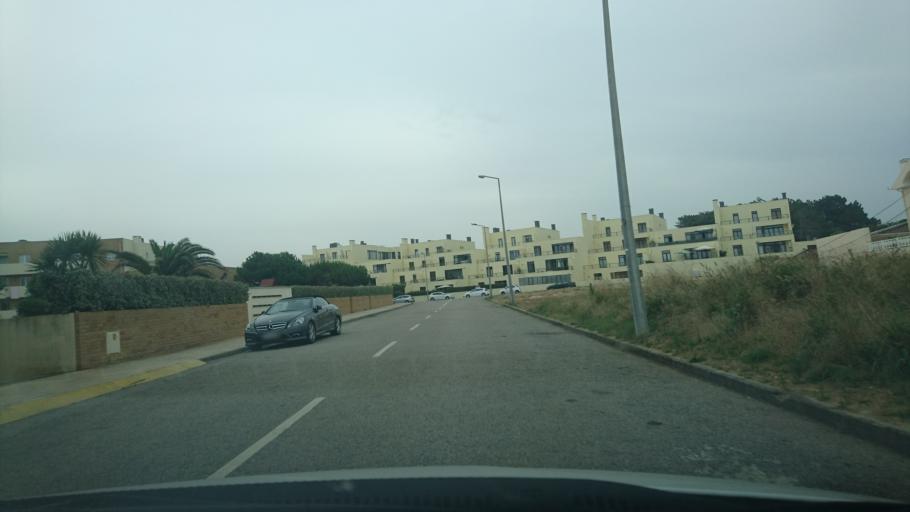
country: PT
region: Aveiro
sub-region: Ovar
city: Esmoriz
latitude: 40.9592
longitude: -8.6517
